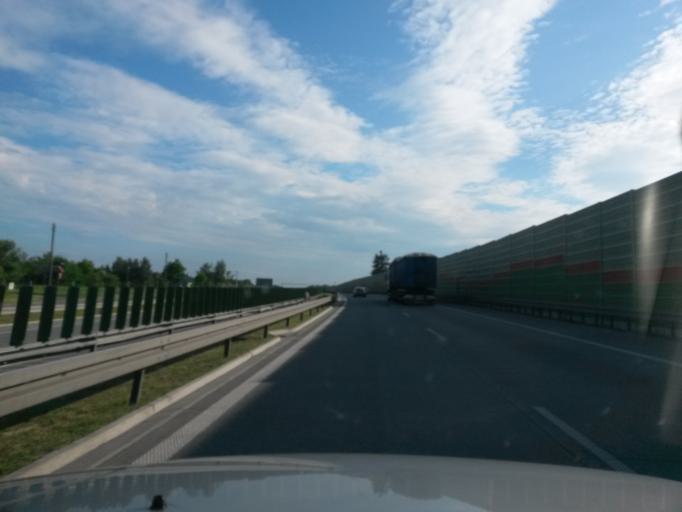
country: PL
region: Lodz Voivodeship
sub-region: Powiat rawski
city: Rawa Mazowiecka
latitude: 51.7444
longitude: 20.2370
